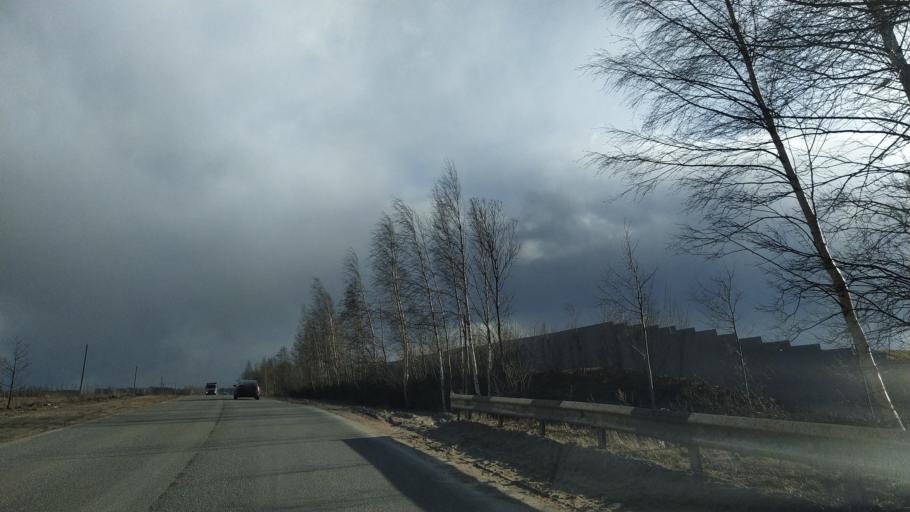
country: RU
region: Leningrad
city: Bugry
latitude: 60.0959
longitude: 30.3905
